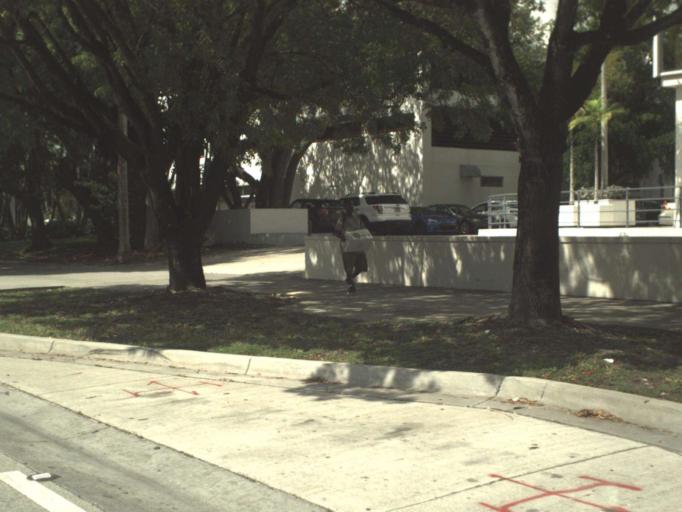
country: US
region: Florida
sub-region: Miami-Dade County
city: Allapattah
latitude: 25.8175
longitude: -80.1884
